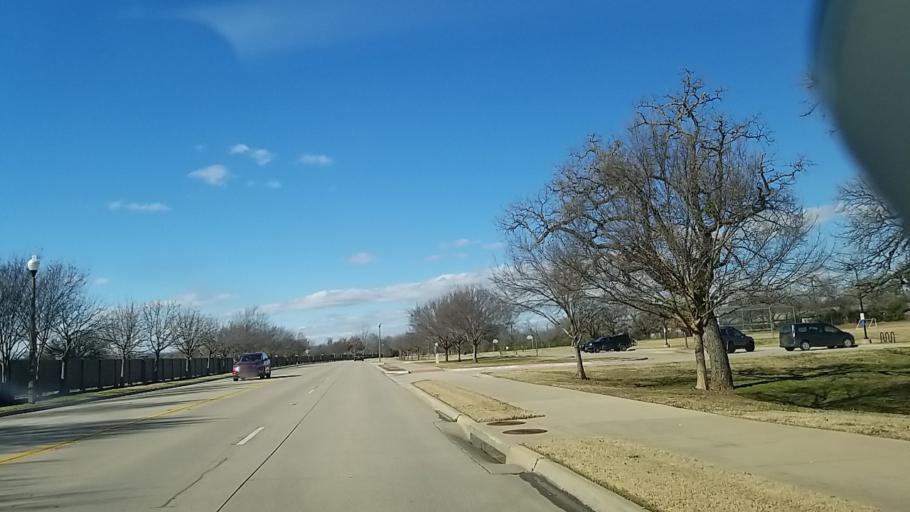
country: US
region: Texas
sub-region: Denton County
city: Corinth
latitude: 33.1697
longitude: -97.0917
